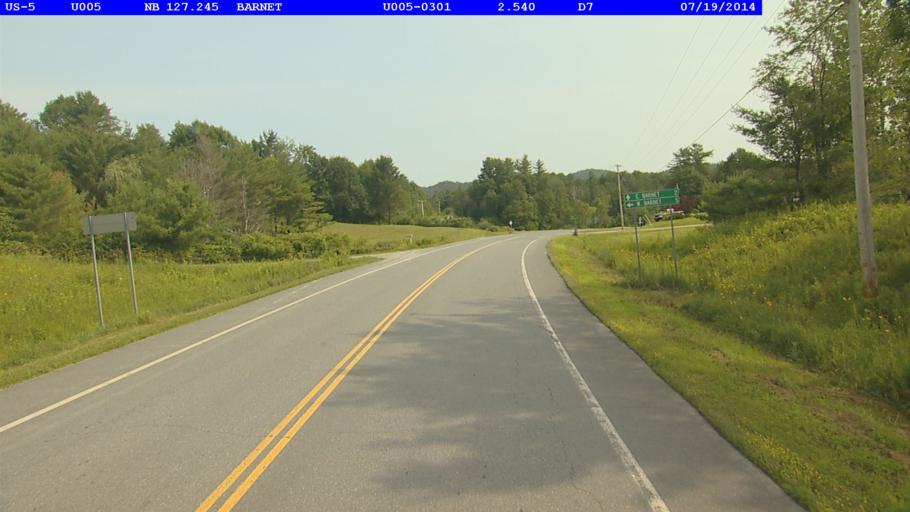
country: US
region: Vermont
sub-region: Caledonia County
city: Saint Johnsbury
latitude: 44.2895
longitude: -72.0588
